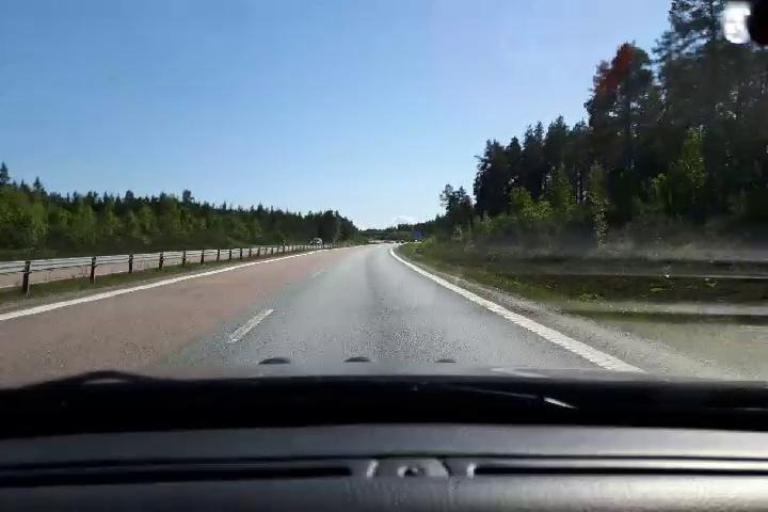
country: SE
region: Gaevleborg
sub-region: Soderhamns Kommun
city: Soderhamn
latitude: 61.3440
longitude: 17.0188
